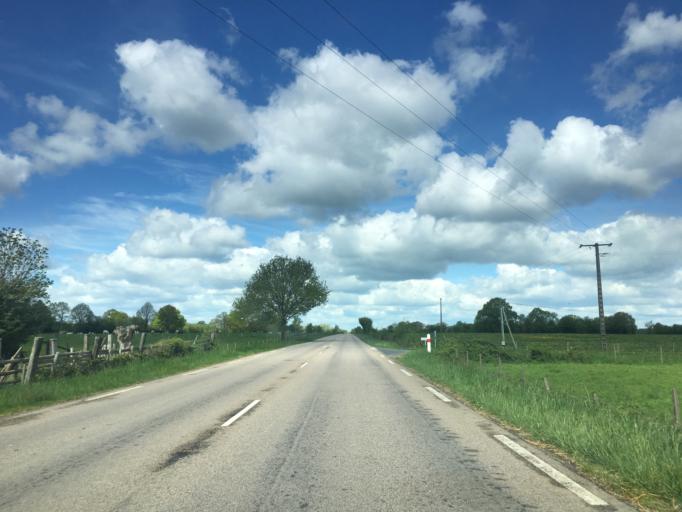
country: FR
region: Lower Normandy
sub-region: Departement de l'Orne
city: Rai
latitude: 48.8309
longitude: 0.5479
